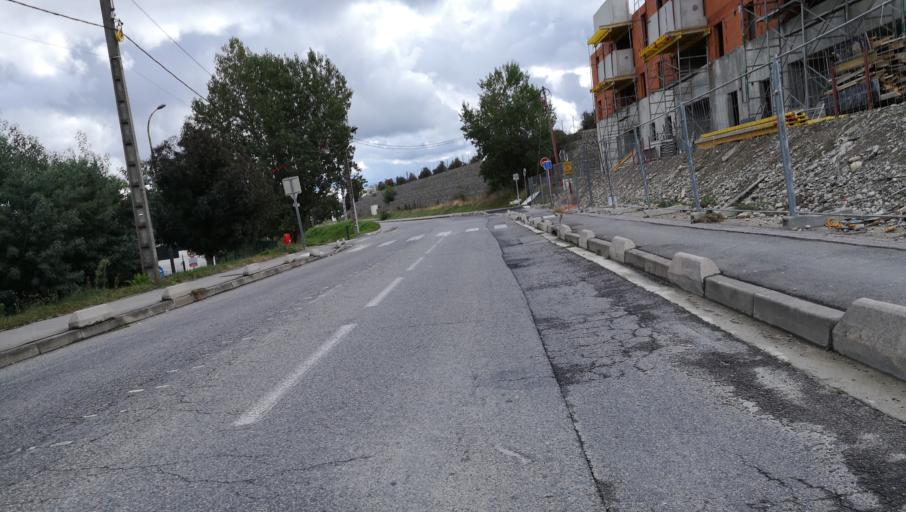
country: FR
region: Midi-Pyrenees
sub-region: Departement de la Haute-Garonne
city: Blagnac
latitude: 43.6126
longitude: 1.4023
